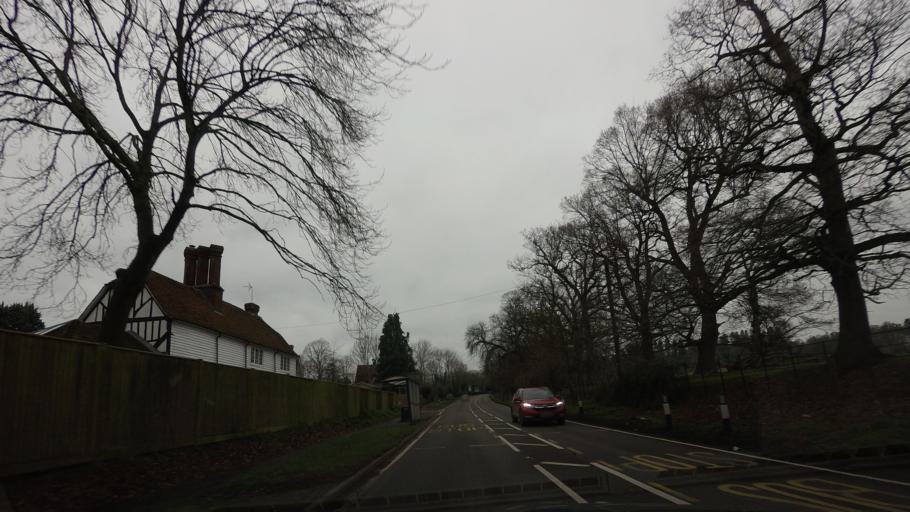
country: GB
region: England
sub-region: Kent
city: Marden
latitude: 51.2173
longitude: 0.5115
